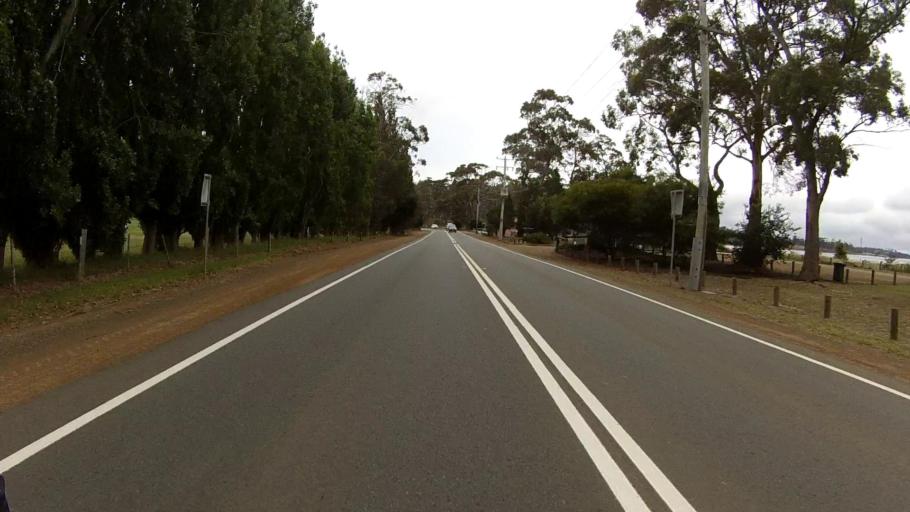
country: AU
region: Tasmania
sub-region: Sorell
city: Sorell
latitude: -42.5489
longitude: 147.8839
